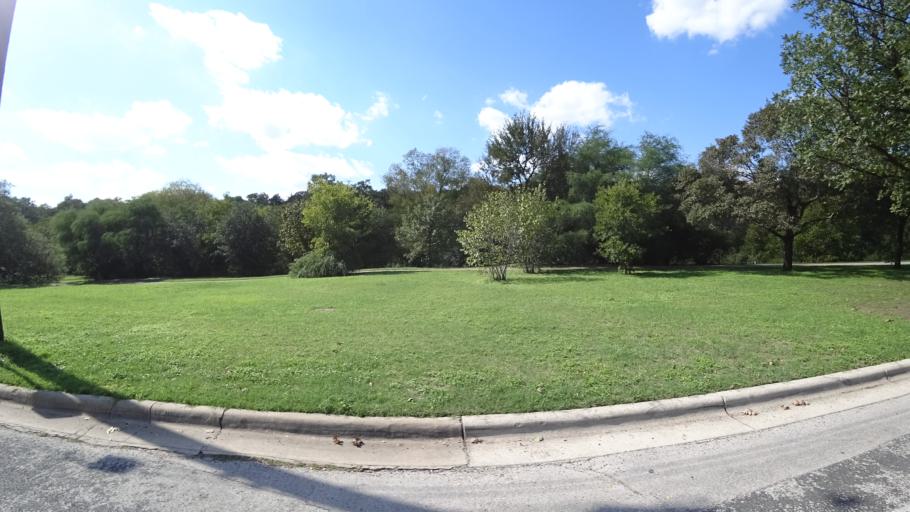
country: US
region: Texas
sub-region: Travis County
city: Austin
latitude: 30.3038
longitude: -97.7489
